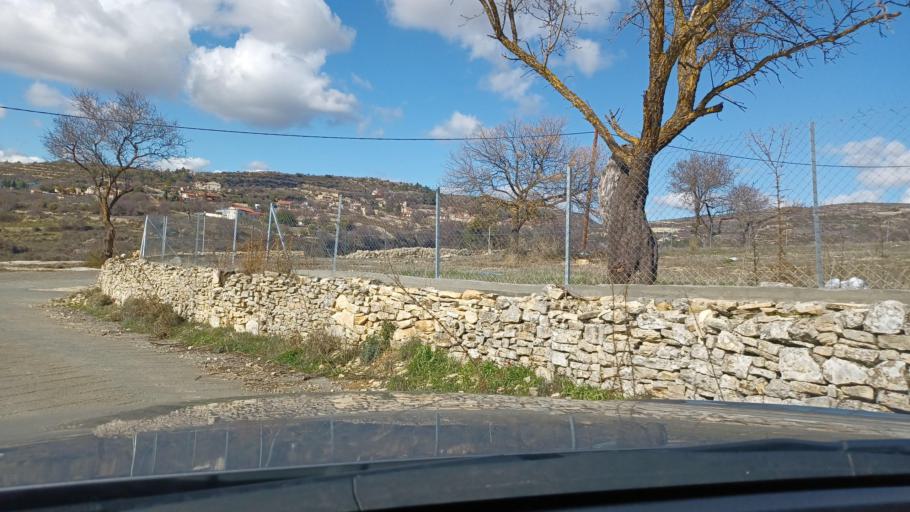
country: CY
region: Limassol
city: Pachna
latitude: 34.8273
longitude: 32.7944
